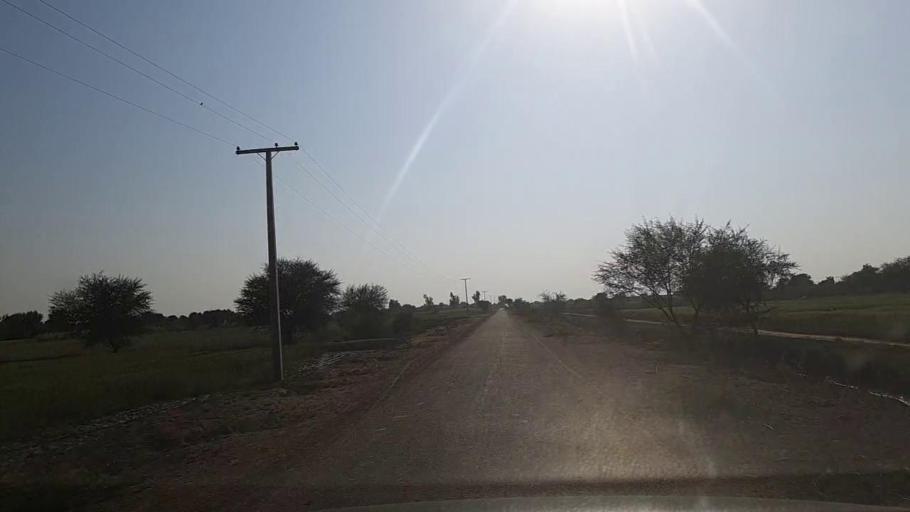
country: PK
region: Sindh
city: Digri
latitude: 25.0253
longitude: 69.2307
